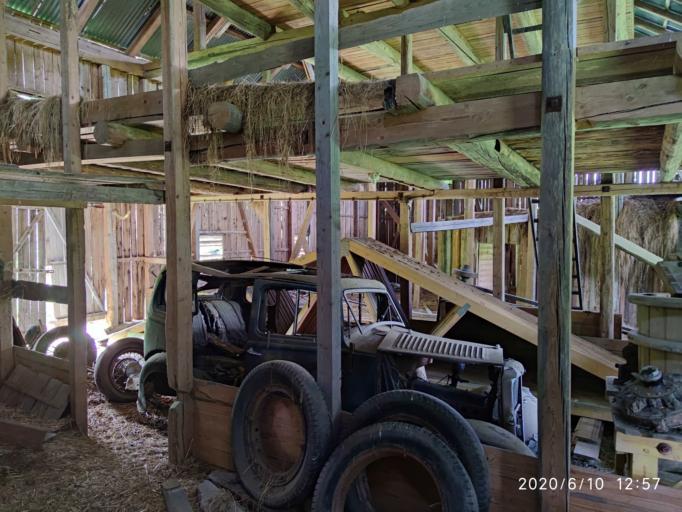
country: NO
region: Oppland
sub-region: Lillehammer
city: Lillehammer
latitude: 61.0025
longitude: 10.4801
